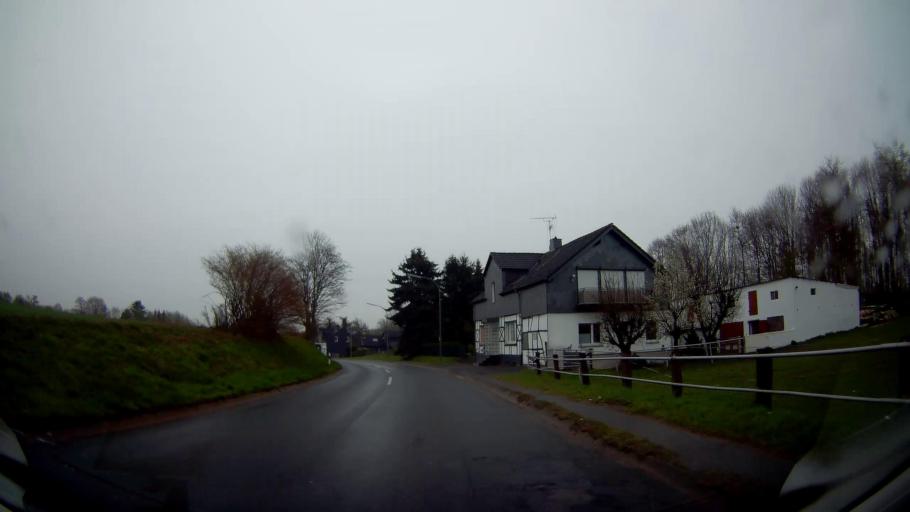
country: DE
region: North Rhine-Westphalia
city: Castrop-Rauxel
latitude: 51.5240
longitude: 7.3074
